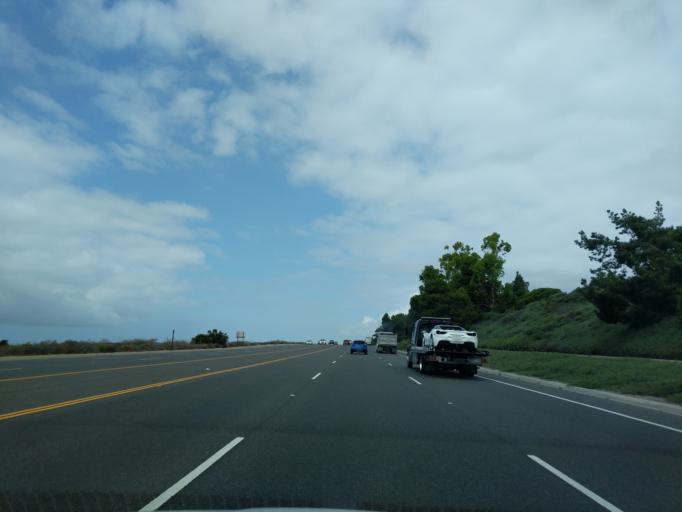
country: US
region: California
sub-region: Orange County
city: San Joaquin Hills
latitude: 33.5792
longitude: -117.8433
